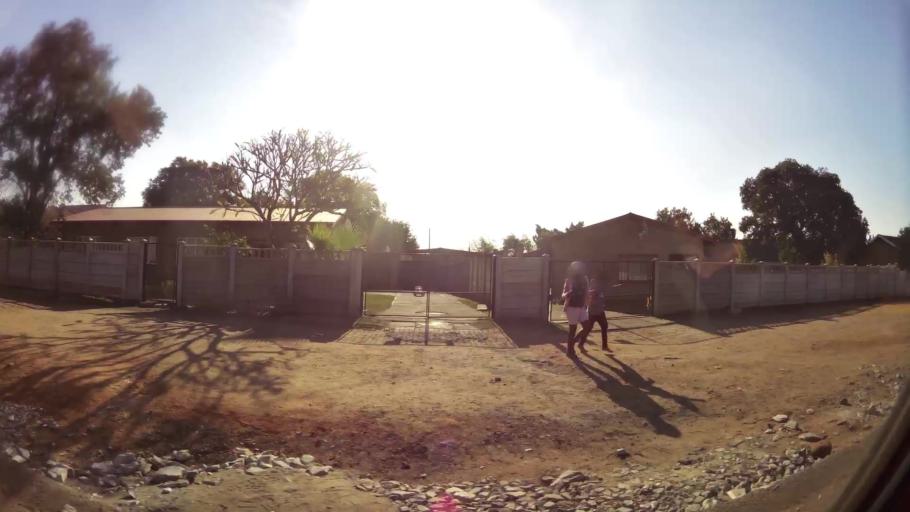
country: ZA
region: North-West
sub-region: Bojanala Platinum District Municipality
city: Rustenburg
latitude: -25.6540
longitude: 27.2309
